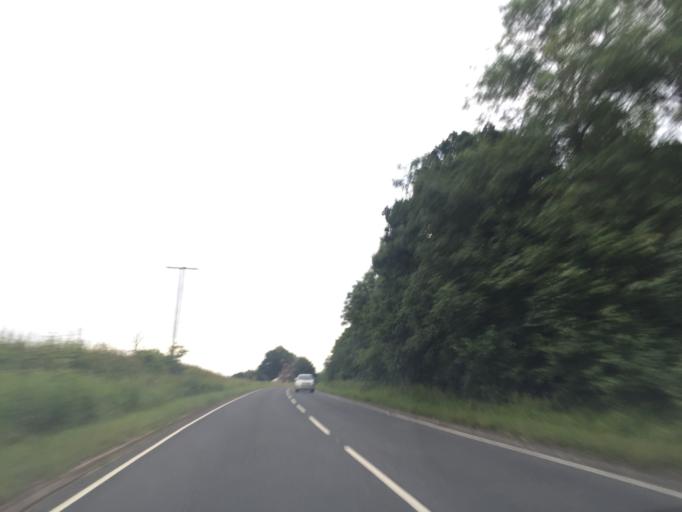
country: GB
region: England
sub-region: Greater London
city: Collier Row
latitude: 51.6614
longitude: 0.1844
